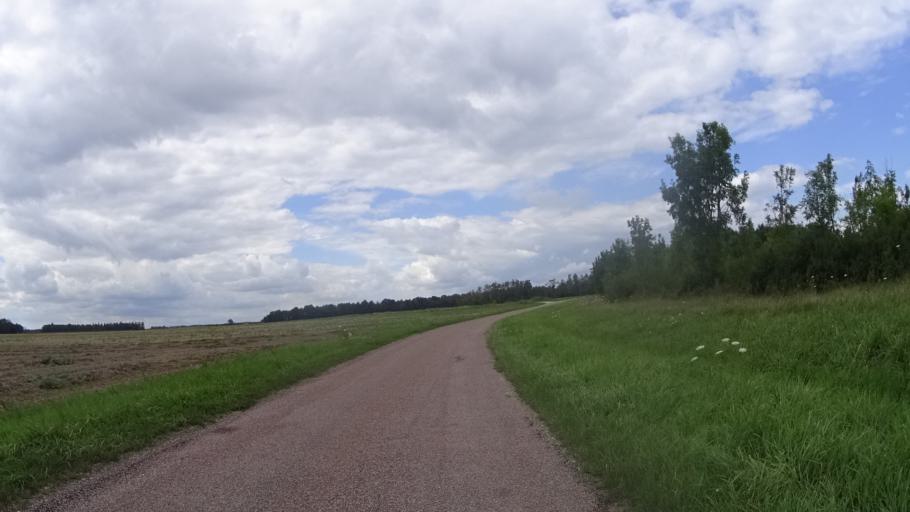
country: FR
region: Champagne-Ardenne
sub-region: Departement de la Haute-Marne
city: Villiers-en-Lieu
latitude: 48.5993
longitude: 4.8607
